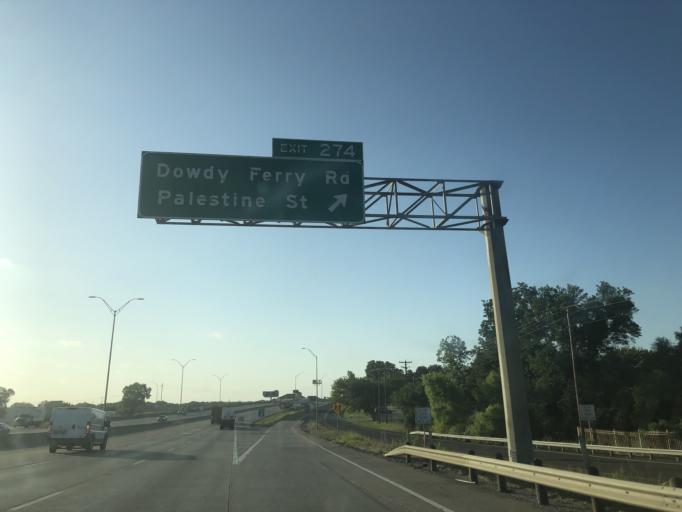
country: US
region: Texas
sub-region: Dallas County
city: Hutchins
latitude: 32.6536
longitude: -96.7128
